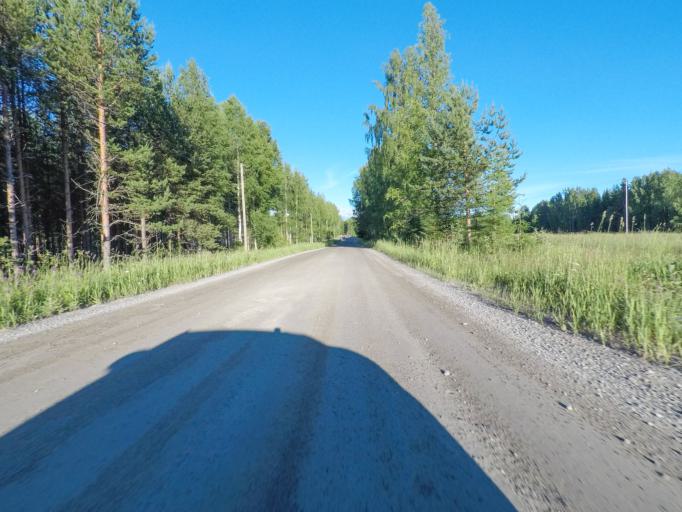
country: FI
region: Northern Savo
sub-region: Kuopio
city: Maaninka
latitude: 62.8782
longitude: 27.2976
